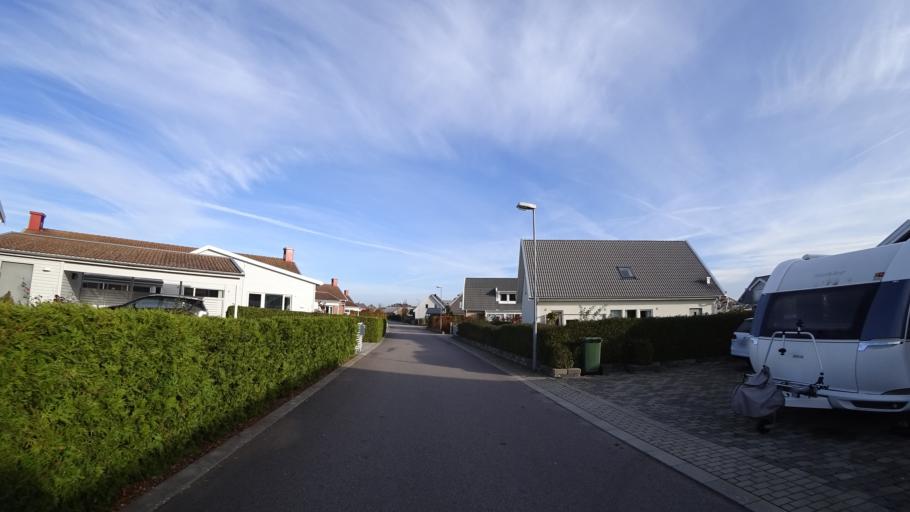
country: SE
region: Skane
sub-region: Staffanstorps Kommun
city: Staffanstorp
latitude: 55.6334
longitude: 13.2216
